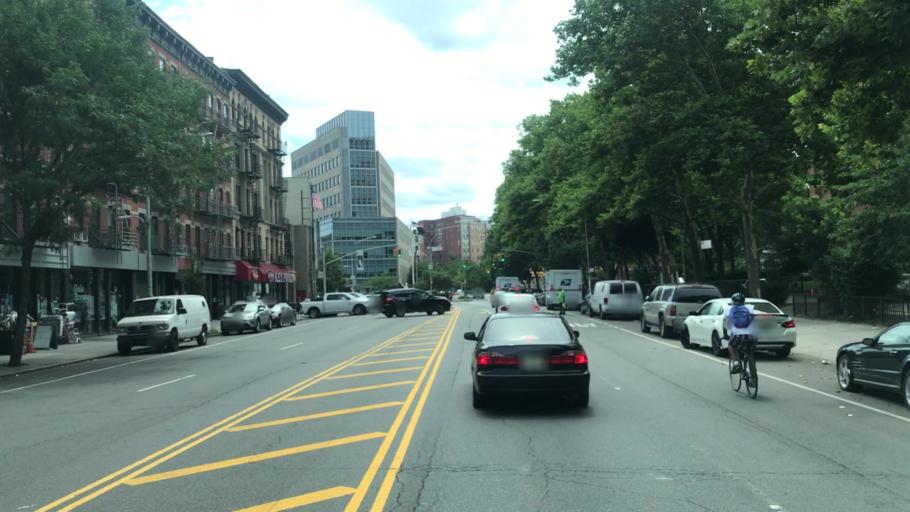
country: US
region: New Jersey
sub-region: Bergen County
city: Edgewater
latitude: 40.8125
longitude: -73.9555
